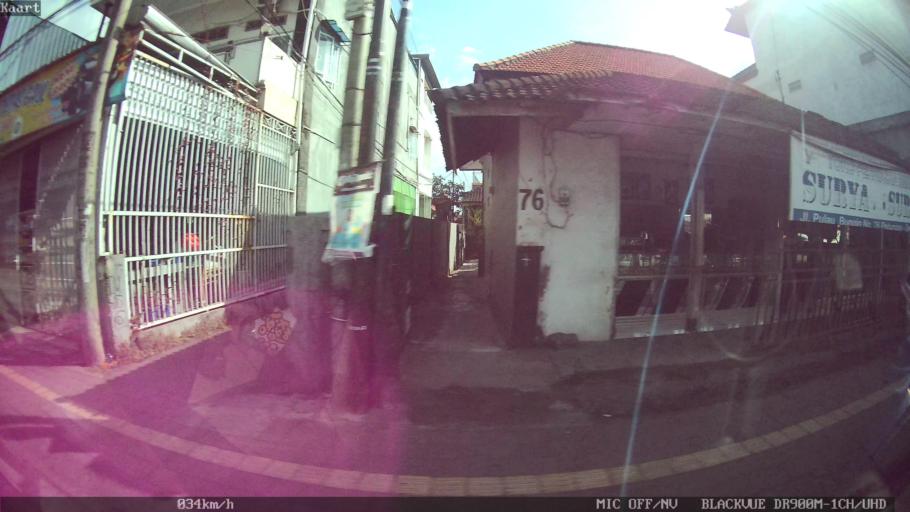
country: ID
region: Bali
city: Karyadharma
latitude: -8.6905
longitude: 115.2024
